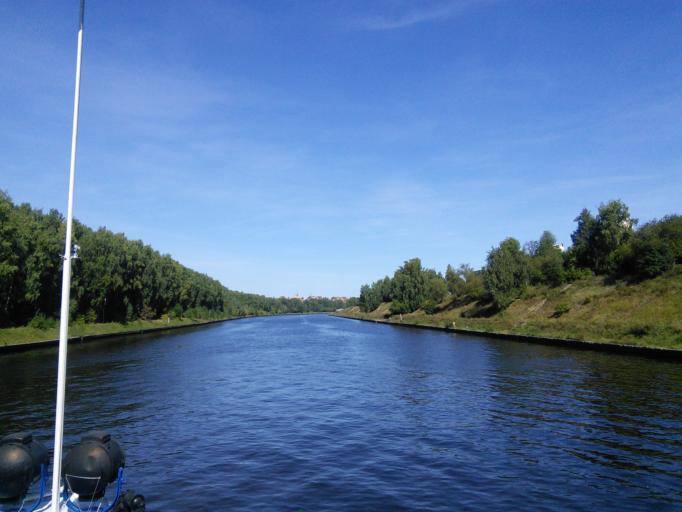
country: RU
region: Moskovskaya
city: Dolgoprudnyy
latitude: 55.9359
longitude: 37.4858
